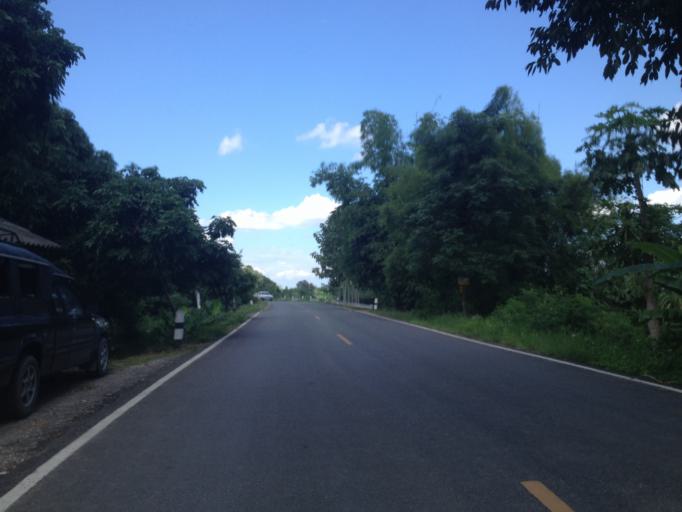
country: TH
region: Chiang Mai
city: Hang Dong
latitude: 18.6494
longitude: 98.9562
